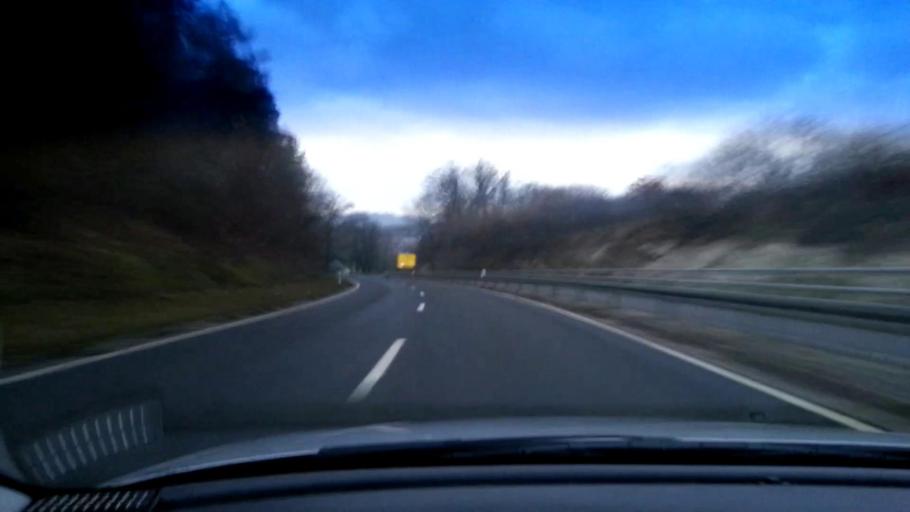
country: DE
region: Bavaria
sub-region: Upper Franconia
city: Frensdorf
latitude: 49.8464
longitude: 10.8779
